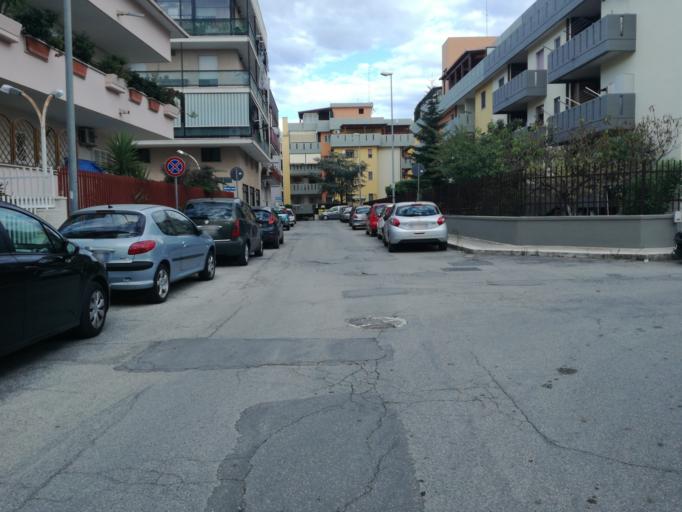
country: IT
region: Apulia
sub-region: Provincia di Bari
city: Triggiano
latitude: 41.0665
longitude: 16.9353
